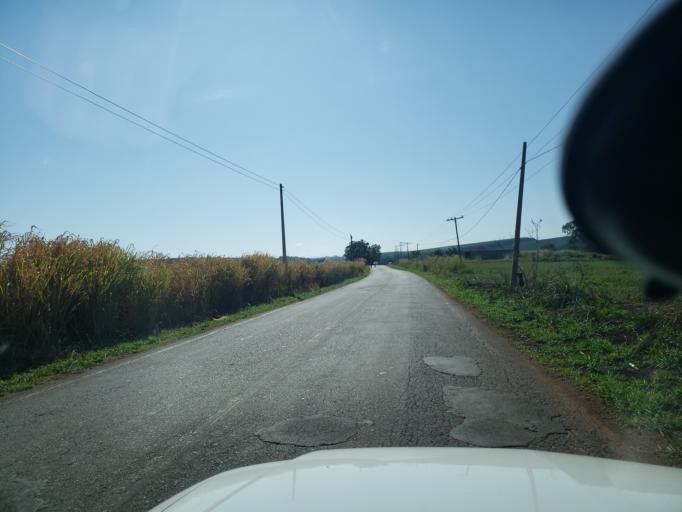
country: BR
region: Sao Paulo
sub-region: Moji-Guacu
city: Mogi-Gaucu
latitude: -22.3385
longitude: -46.8855
